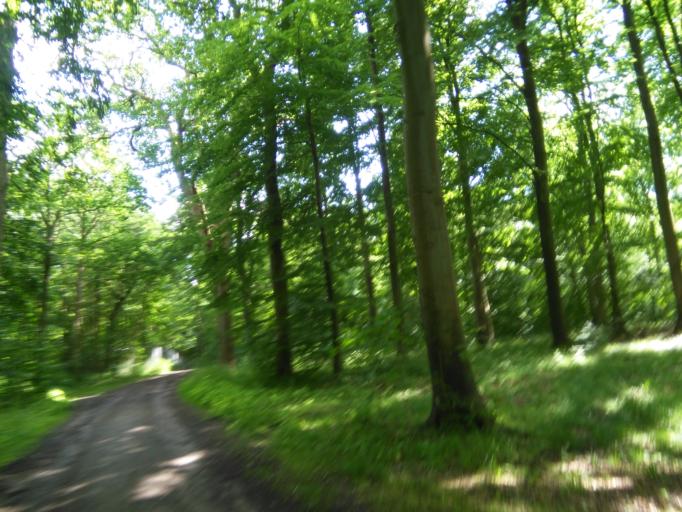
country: DK
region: Central Jutland
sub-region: Arhus Kommune
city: Arhus
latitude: 56.1234
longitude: 10.2114
